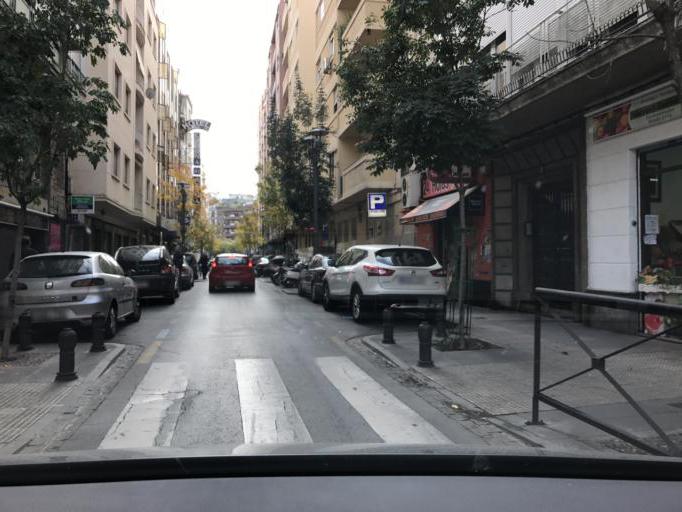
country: ES
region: Andalusia
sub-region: Provincia de Granada
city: Granada
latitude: 37.1700
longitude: -3.6043
